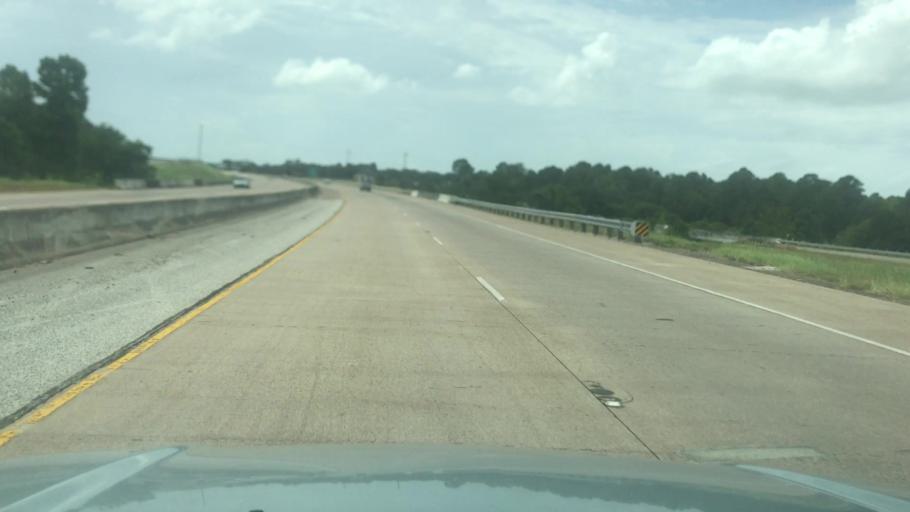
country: US
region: Texas
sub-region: Fayette County
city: La Grange
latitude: 29.9223
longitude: -96.8628
